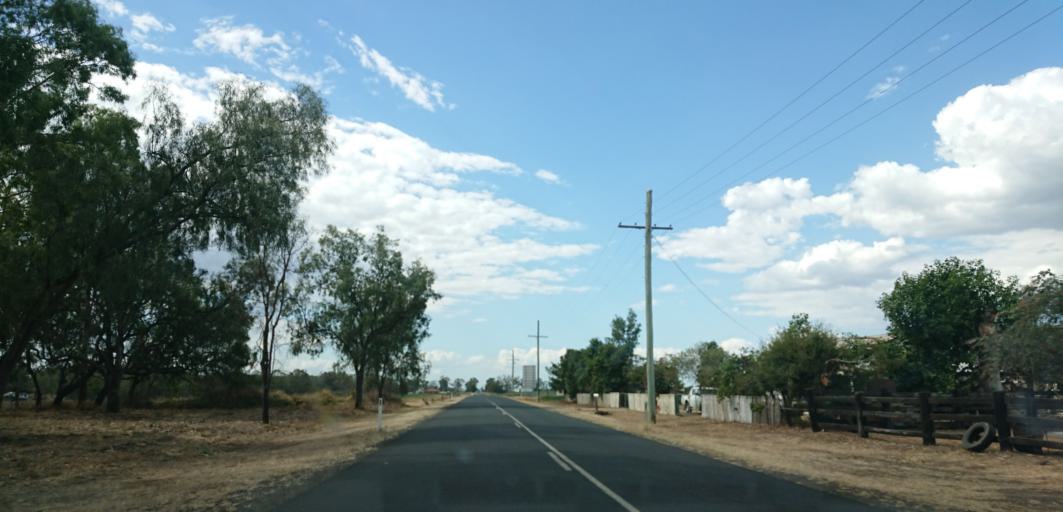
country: AU
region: Queensland
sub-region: Lockyer Valley
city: Gatton
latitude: -27.6063
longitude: 152.2111
